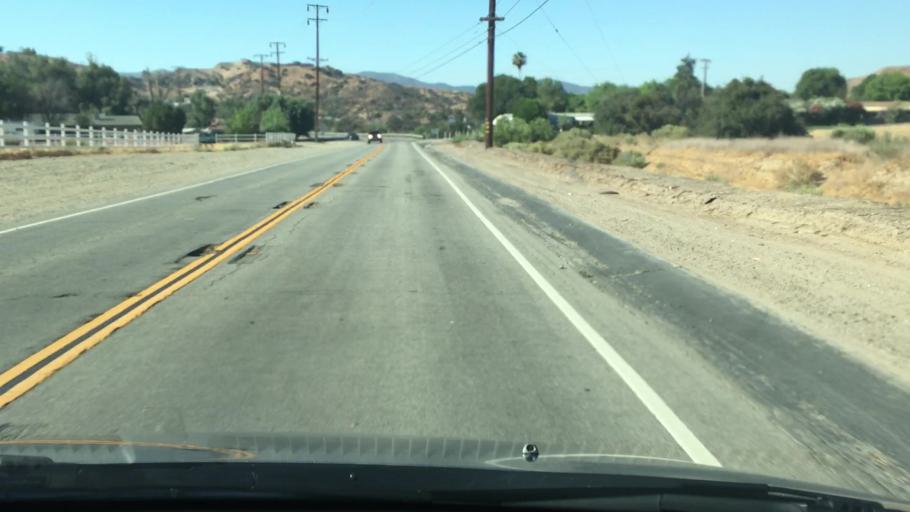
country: US
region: California
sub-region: Los Angeles County
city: Agua Dulce
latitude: 34.4575
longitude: -118.4214
